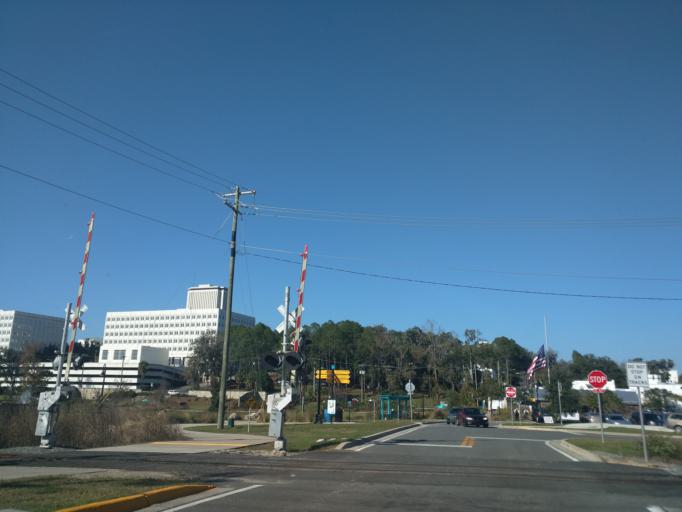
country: US
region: Florida
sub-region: Leon County
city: Tallahassee
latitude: 30.4328
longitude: -84.2782
